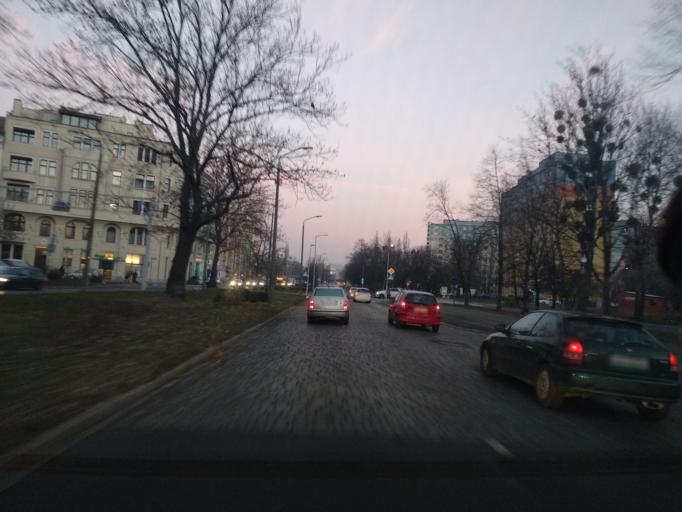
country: PL
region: Lower Silesian Voivodeship
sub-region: Powiat wroclawski
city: Wroclaw
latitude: 51.0978
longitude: 17.0146
